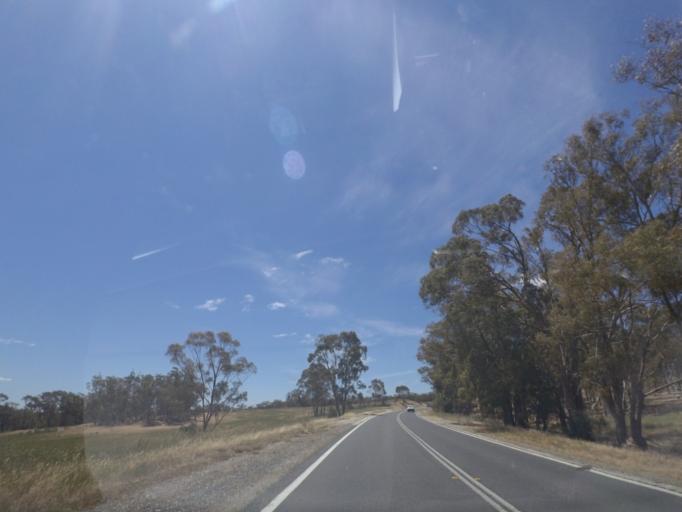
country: AU
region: Victoria
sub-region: Mount Alexander
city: Castlemaine
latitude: -37.1681
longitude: 144.1470
